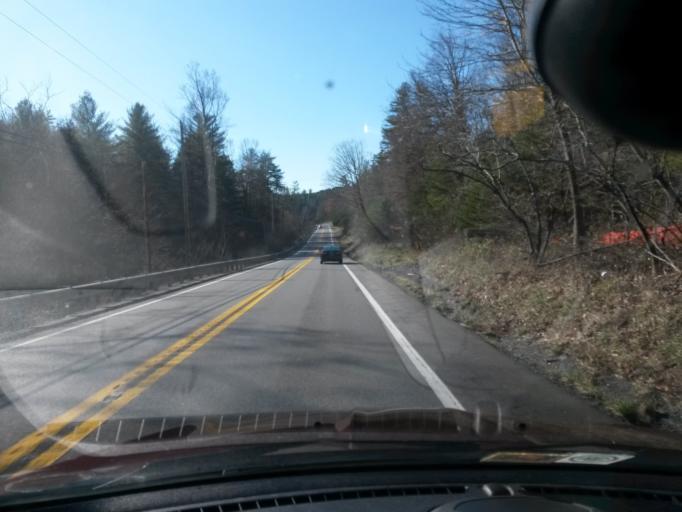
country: US
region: Virginia
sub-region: Alleghany County
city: Clifton Forge
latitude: 37.7091
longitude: -79.8135
